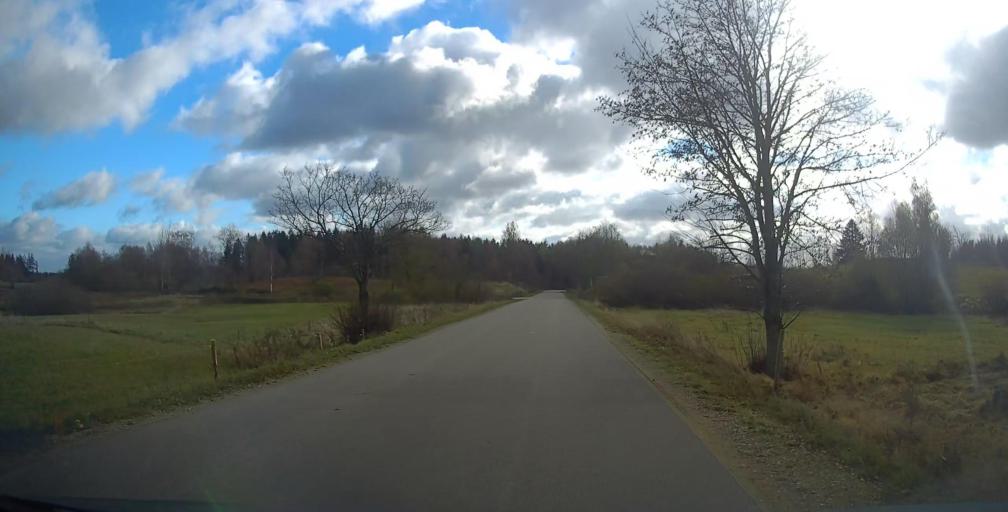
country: PL
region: Podlasie
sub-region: Suwalki
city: Suwalki
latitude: 54.3129
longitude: 22.8790
